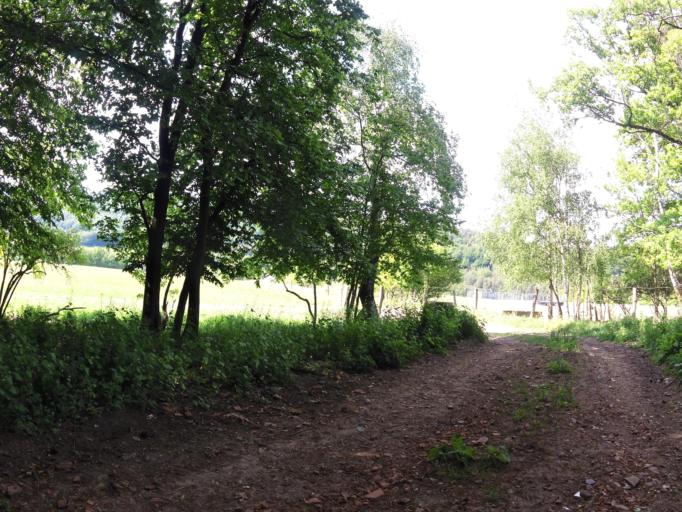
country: DE
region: Thuringia
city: Seebach
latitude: 50.9574
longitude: 10.4285
